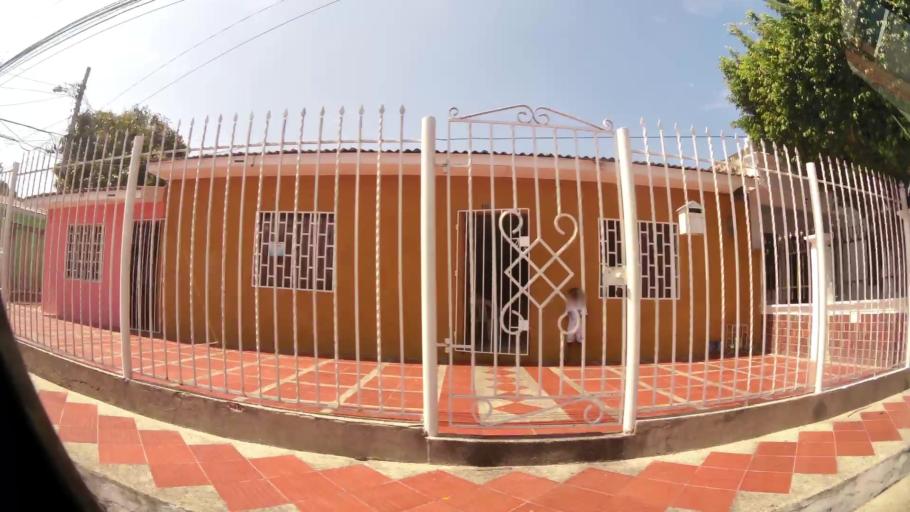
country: CO
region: Atlantico
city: Barranquilla
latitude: 10.9667
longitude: -74.8098
